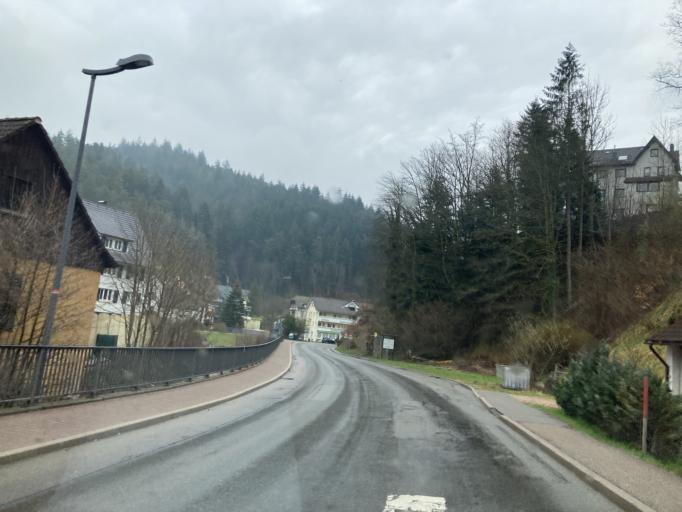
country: DE
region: Baden-Wuerttemberg
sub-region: Freiburg Region
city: Lauterbach/Schwarzwald
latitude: 48.2264
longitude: 8.3549
